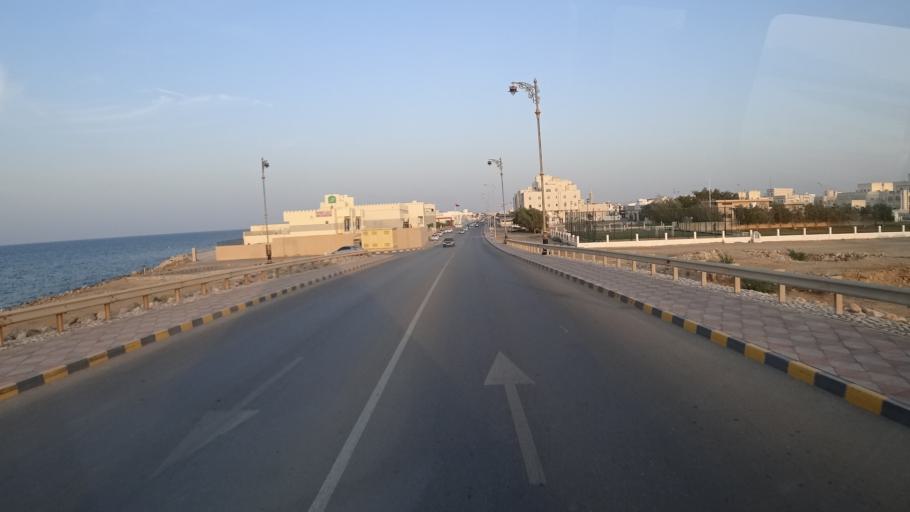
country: OM
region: Ash Sharqiyah
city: Sur
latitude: 22.5964
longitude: 59.4910
